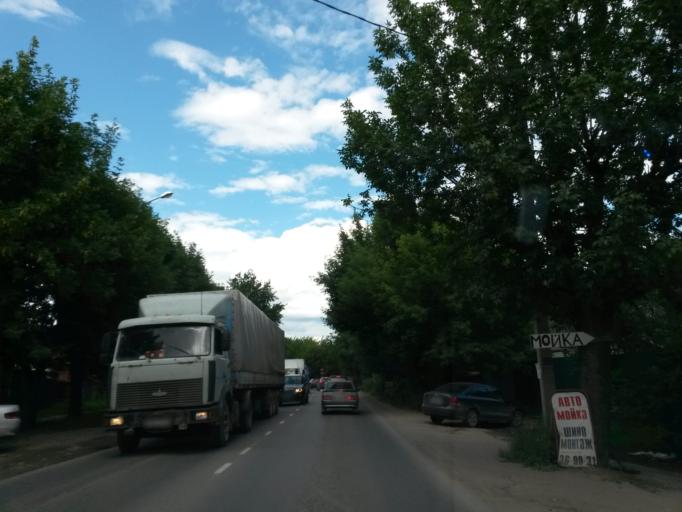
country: RU
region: Ivanovo
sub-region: Gorod Ivanovo
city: Ivanovo
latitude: 56.9923
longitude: 40.9528
